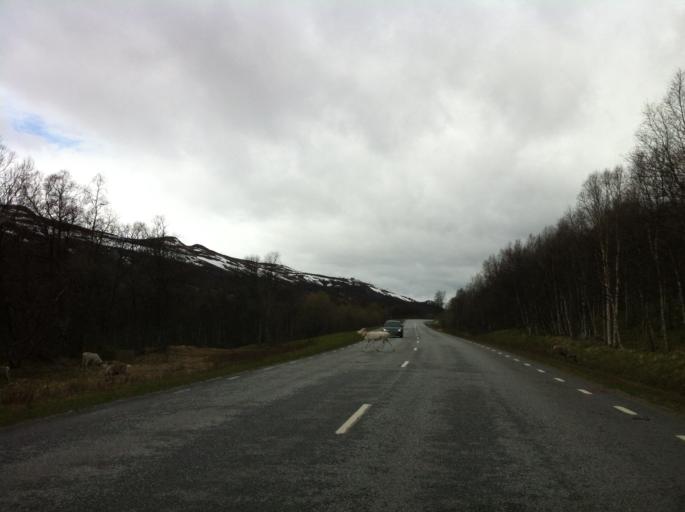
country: NO
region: Sor-Trondelag
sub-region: Tydal
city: Aas
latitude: 62.5566
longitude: 12.2731
